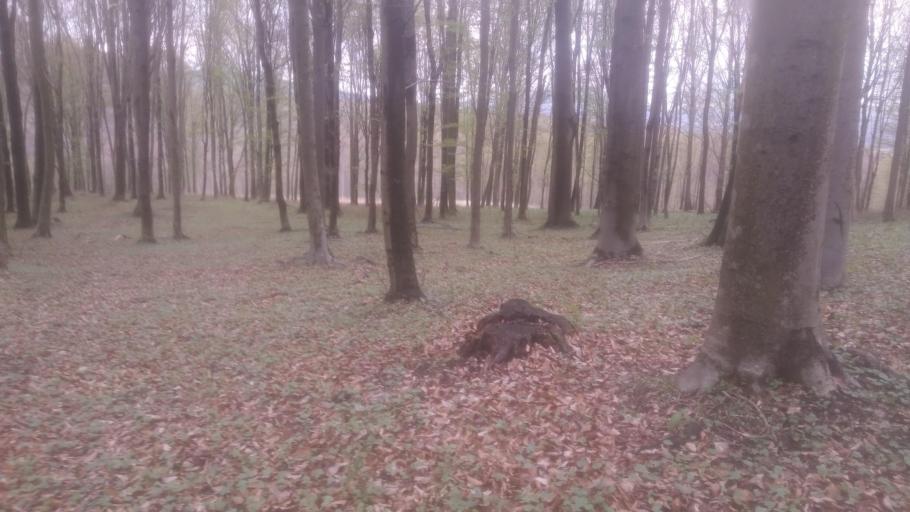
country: HU
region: Veszprem
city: Herend
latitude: 47.2251
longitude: 17.7193
